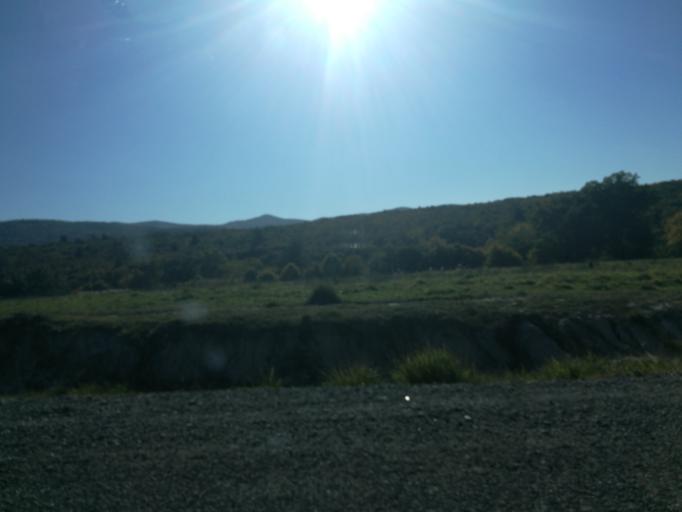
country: RO
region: Brasov
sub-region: Comuna Dumbravita
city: Dumbravita
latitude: 45.7517
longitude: 25.3954
